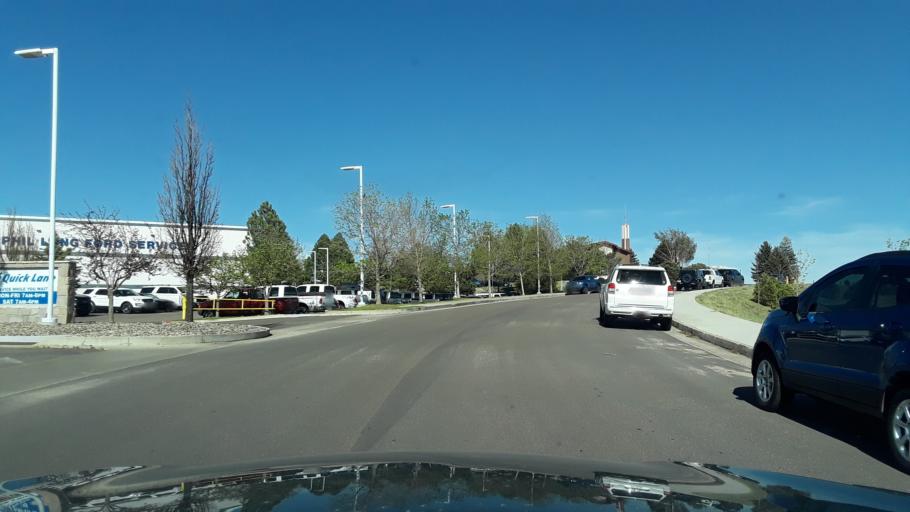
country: US
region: Colorado
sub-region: El Paso County
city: Air Force Academy
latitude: 38.9517
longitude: -104.7965
